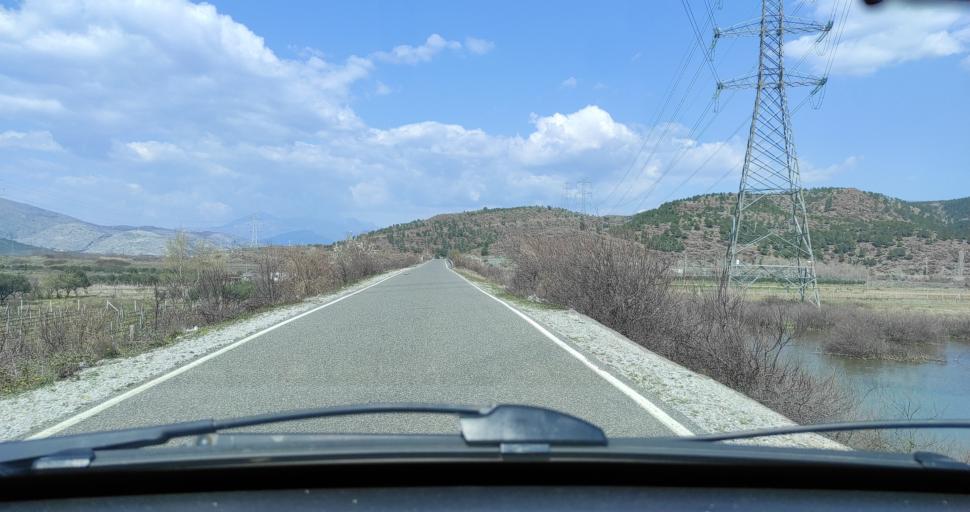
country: AL
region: Shkoder
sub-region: Rrethi i Shkodres
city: Hajmel
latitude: 41.9743
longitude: 19.6448
